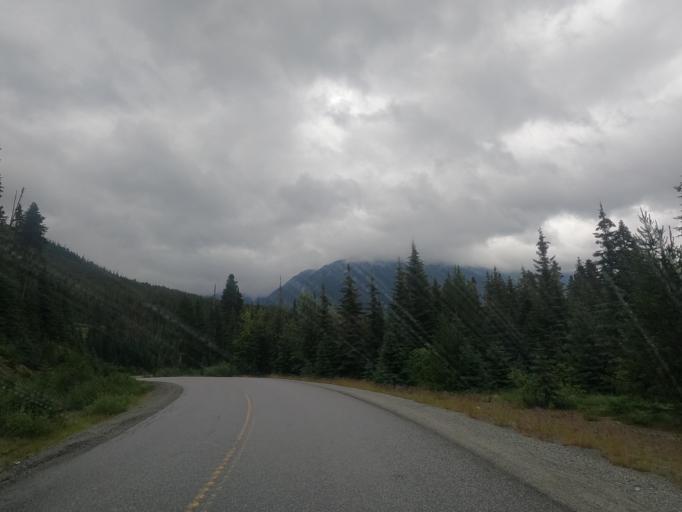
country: CA
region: British Columbia
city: Pemberton
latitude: 50.3777
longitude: -122.4877
